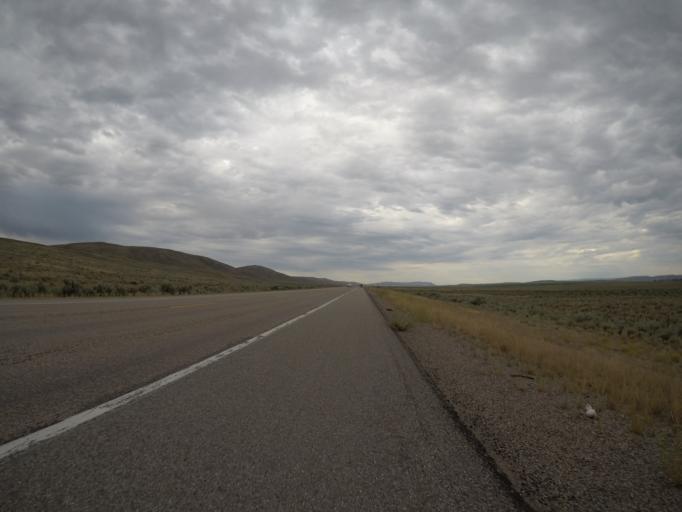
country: US
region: Utah
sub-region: Rich County
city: Randolph
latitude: 41.8762
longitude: -110.9660
